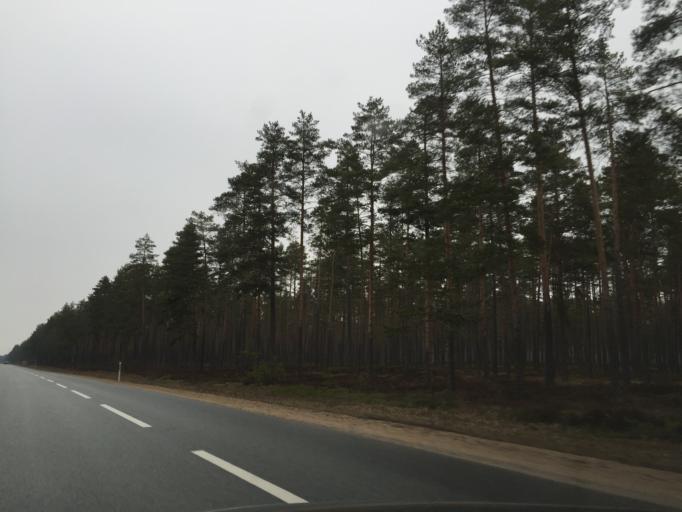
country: LV
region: Carnikava
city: Carnikava
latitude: 57.1599
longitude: 24.3461
